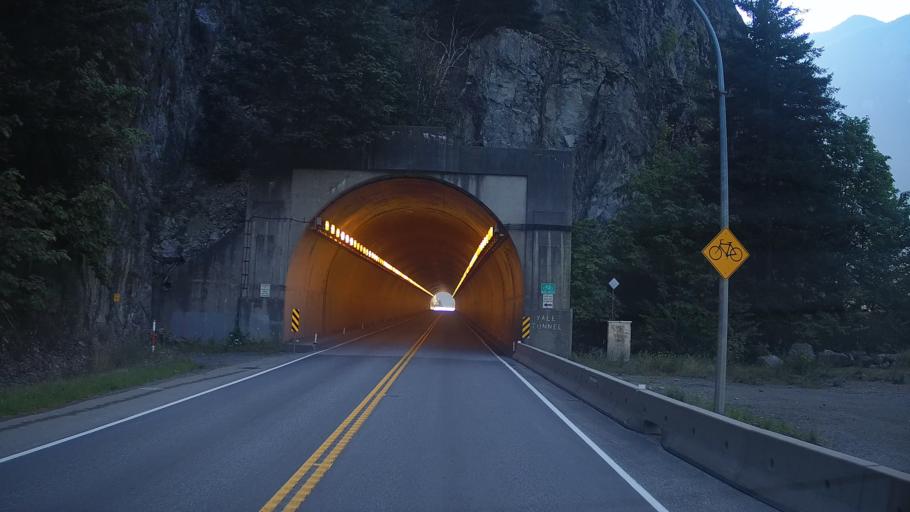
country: CA
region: British Columbia
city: Hope
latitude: 49.5630
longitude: -121.4146
